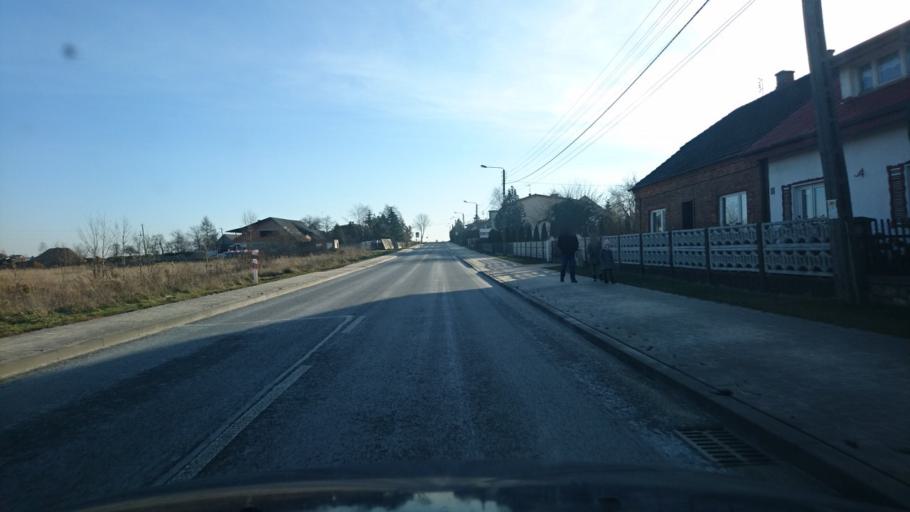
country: PL
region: Silesian Voivodeship
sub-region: Powiat klobucki
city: Starokrzepice
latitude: 51.0224
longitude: 18.6500
